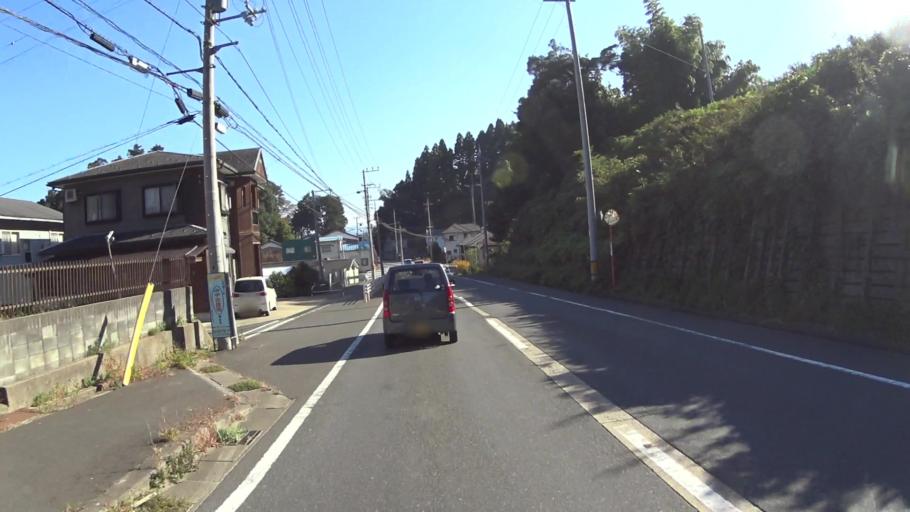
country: JP
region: Kyoto
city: Miyazu
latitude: 35.6325
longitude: 135.0544
